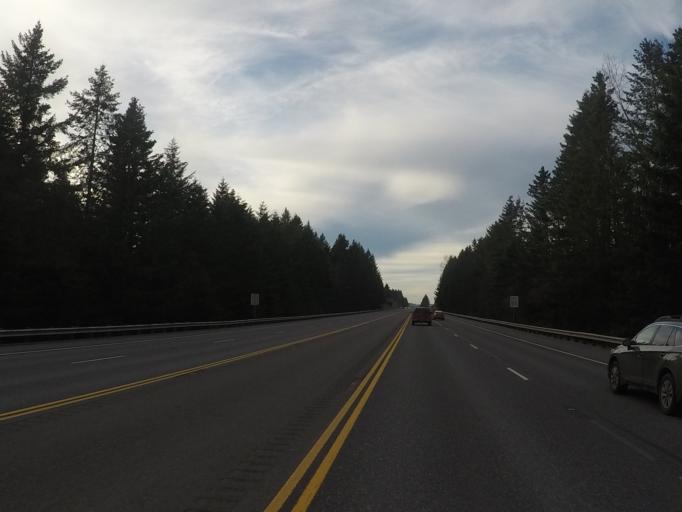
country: US
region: Oregon
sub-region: Clackamas County
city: Sandy
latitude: 45.4113
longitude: -122.3060
